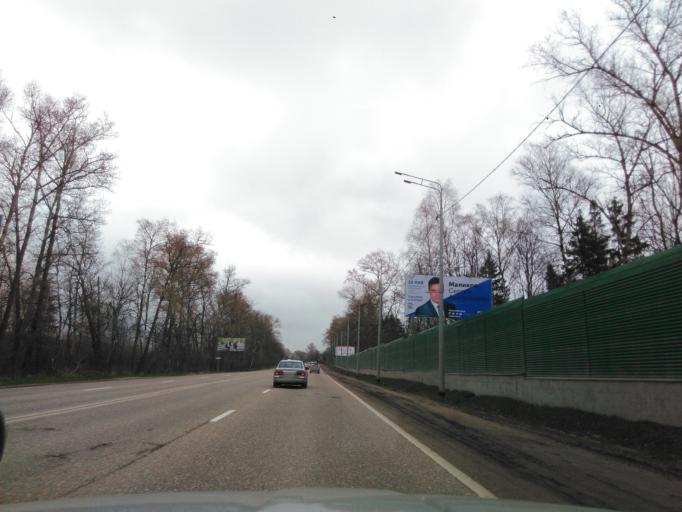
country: RU
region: Moskovskaya
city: Opalikha
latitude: 55.8399
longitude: 37.2309
